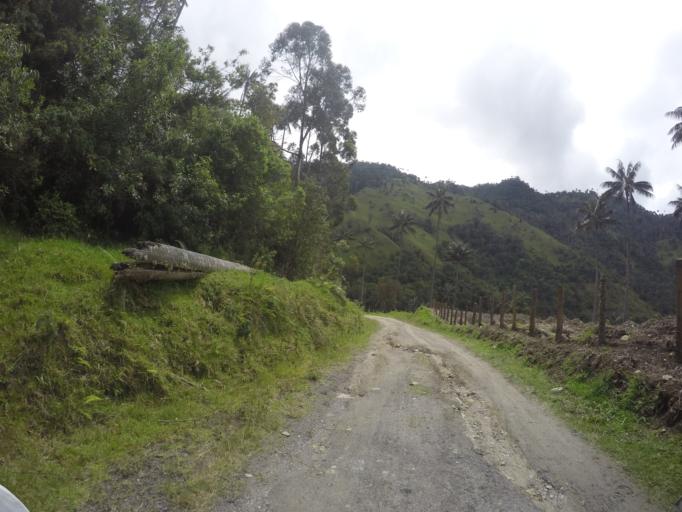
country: CO
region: Tolima
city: Cajamarca
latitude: 4.5357
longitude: -75.4433
